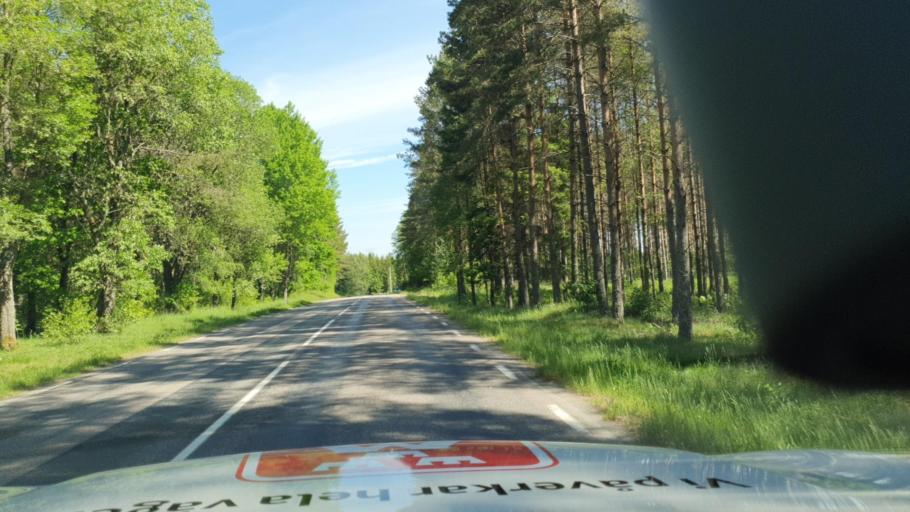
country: SE
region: Vaestra Goetaland
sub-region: Herrljunga Kommun
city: Herrljunga
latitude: 57.9828
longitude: 13.0832
